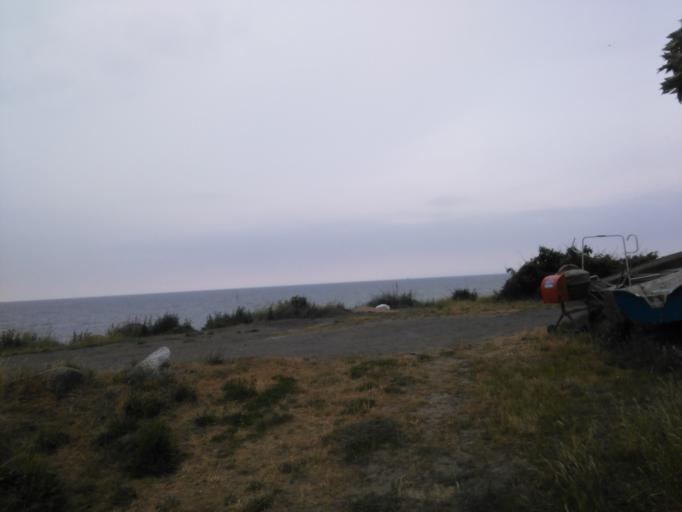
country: DK
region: Capital Region
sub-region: Bornholm Kommune
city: Akirkeby
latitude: 55.0413
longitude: 14.8322
